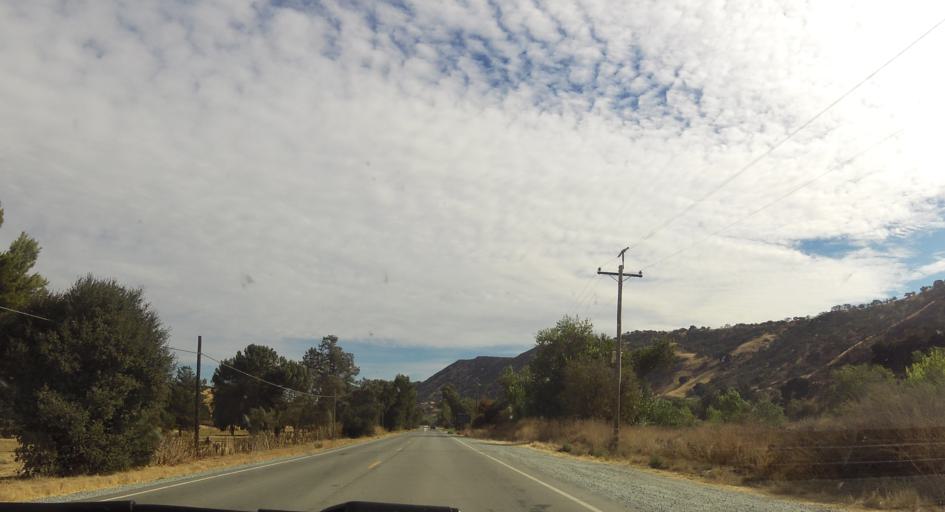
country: US
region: California
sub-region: San Benito County
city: Ridgemark
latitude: 36.7777
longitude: -121.3113
